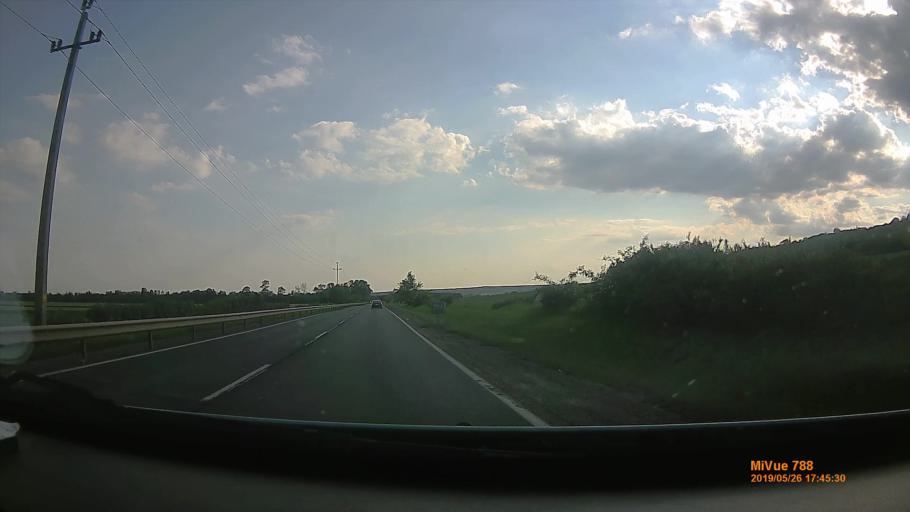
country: HU
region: Borsod-Abauj-Zemplen
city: Aszalo
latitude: 48.2167
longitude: 20.9489
